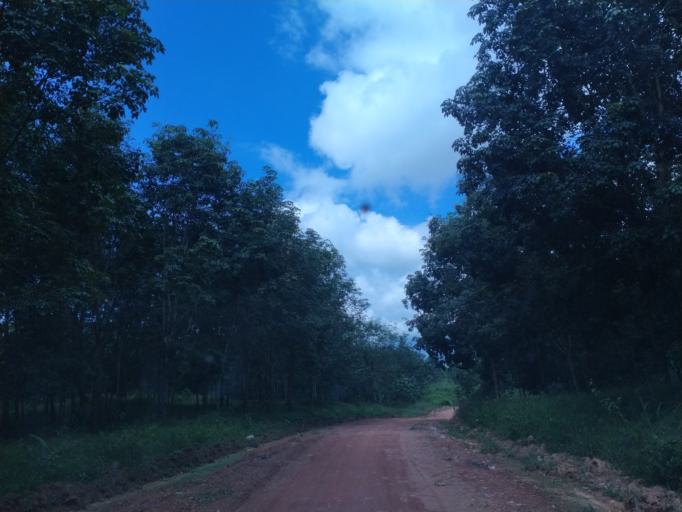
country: TH
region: Nong Khai
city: Rattanawapi
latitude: 18.6397
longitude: 102.9241
